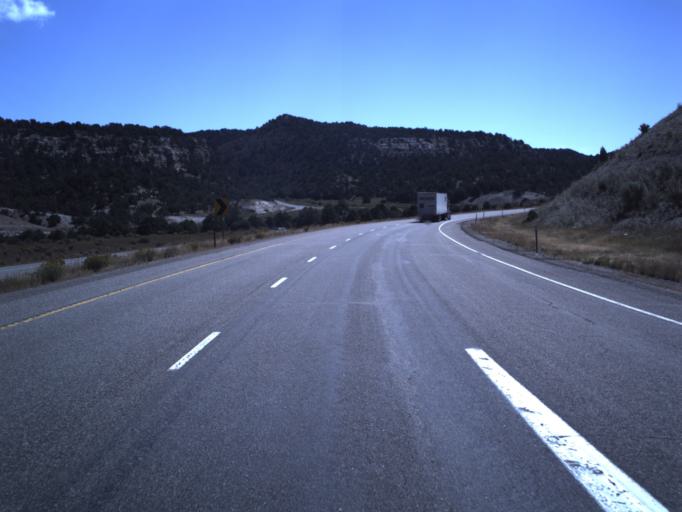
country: US
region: Utah
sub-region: Sevier County
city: Salina
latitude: 38.8764
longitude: -111.5568
